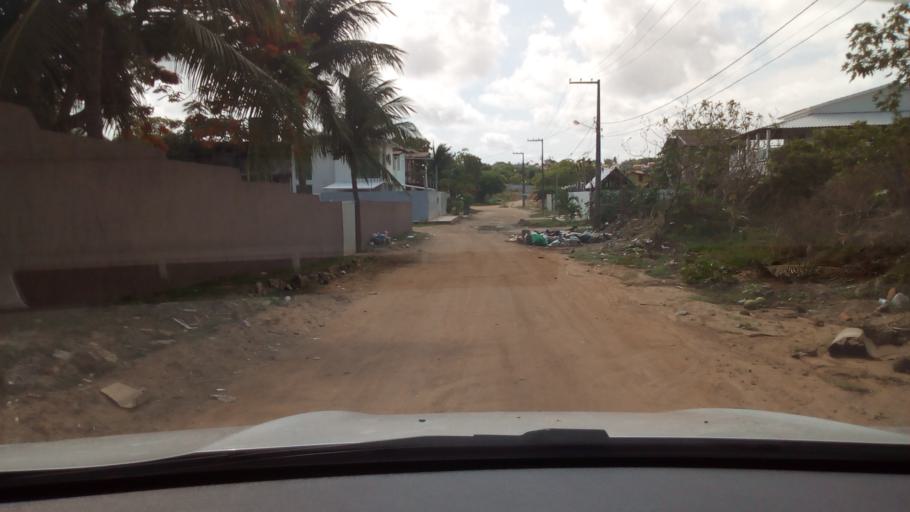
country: BR
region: Paraiba
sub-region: Conde
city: Conde
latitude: -7.2941
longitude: -34.8024
